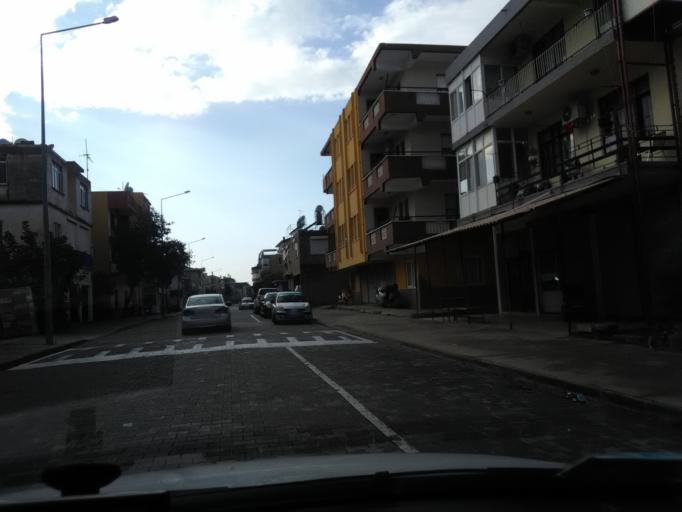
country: TR
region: Antalya
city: Gazipasa
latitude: 36.2699
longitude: 32.3258
